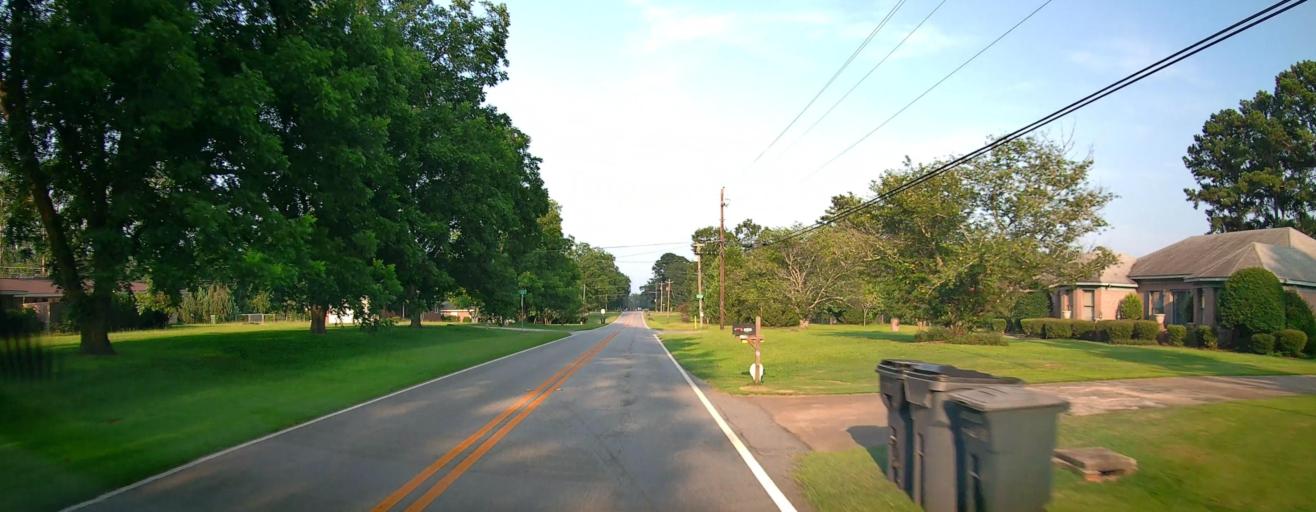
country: US
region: Georgia
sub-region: Houston County
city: Centerville
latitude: 32.7324
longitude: -83.6924
